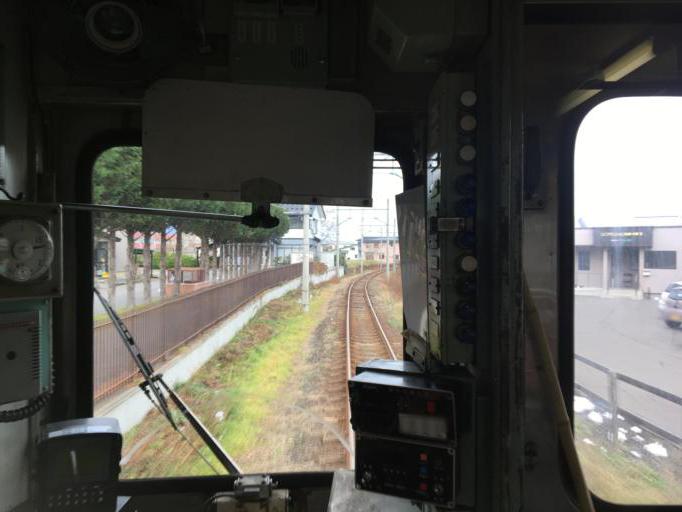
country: JP
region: Aomori
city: Hirosaki
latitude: 40.5730
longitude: 140.4744
